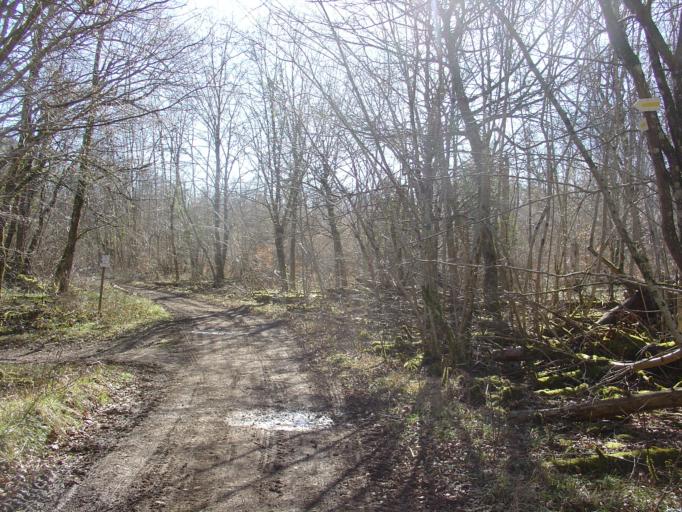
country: FR
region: Lorraine
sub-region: Departement de Meurthe-et-Moselle
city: Blenod-les-Toul
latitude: 48.6166
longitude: 5.8296
